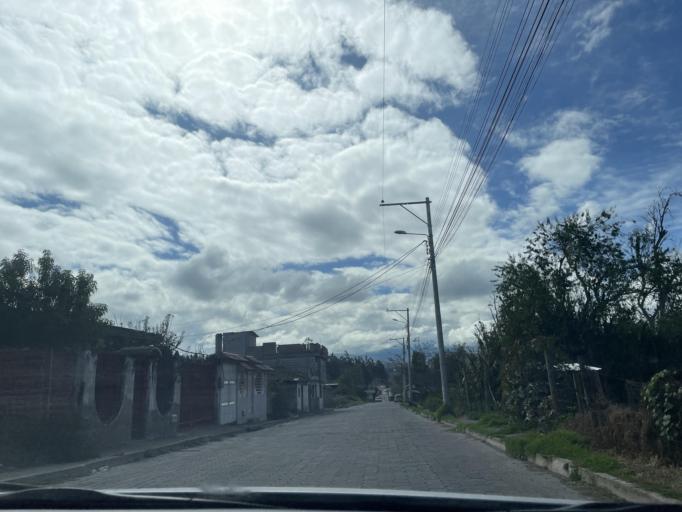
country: EC
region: Chimborazo
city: Guano
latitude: -1.6070
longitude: -78.6260
